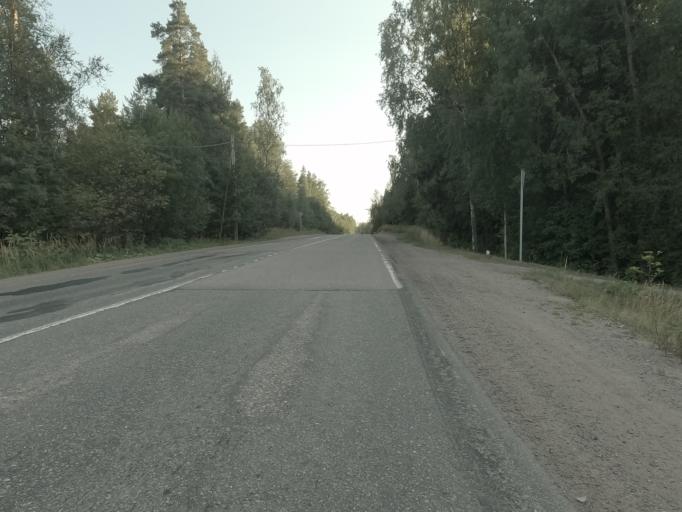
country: RU
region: Leningrad
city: Vyborg
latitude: 60.7425
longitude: 28.7667
